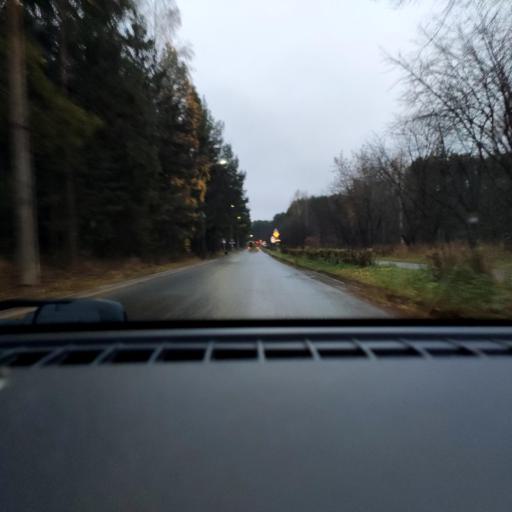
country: RU
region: Perm
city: Perm
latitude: 58.0528
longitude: 56.2143
